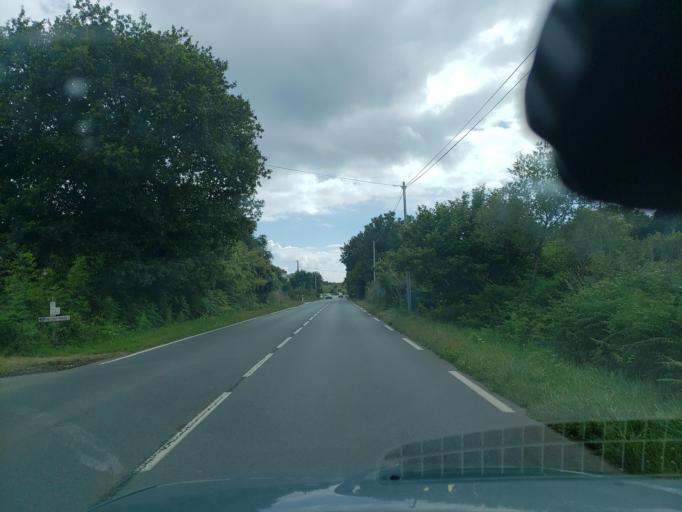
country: FR
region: Brittany
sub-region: Departement du Finistere
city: Plomeur
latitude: 47.8326
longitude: -4.2879
